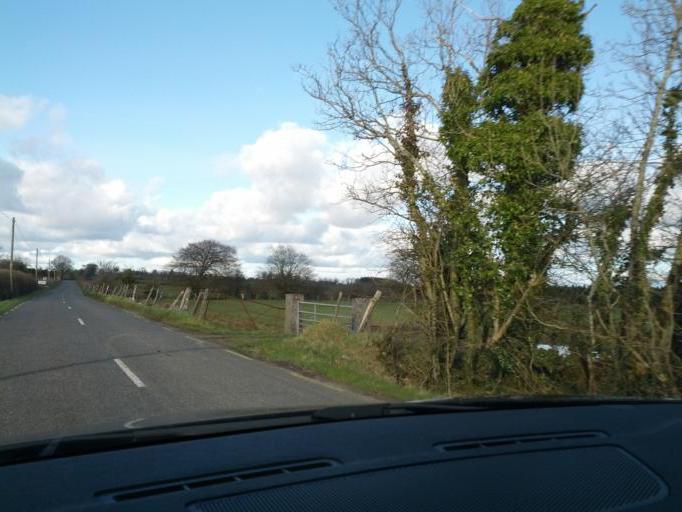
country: IE
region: Connaught
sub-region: Roscommon
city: Castlerea
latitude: 53.5204
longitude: -8.5755
